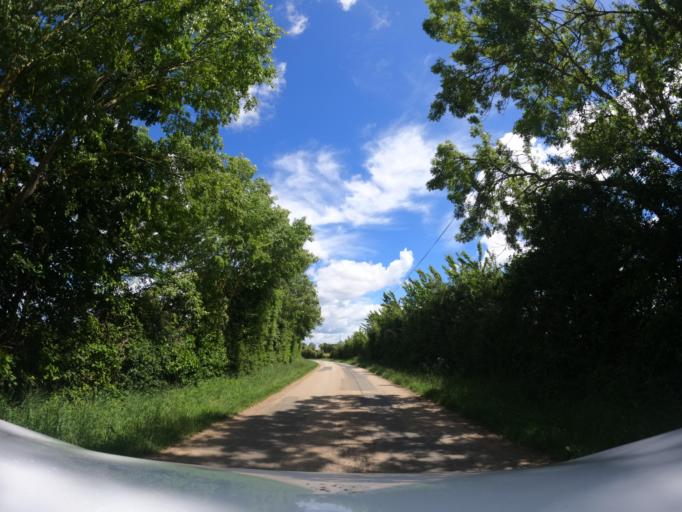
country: FR
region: Pays de la Loire
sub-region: Departement de la Vendee
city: Le Champ-Saint-Pere
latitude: 46.4769
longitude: -1.3152
